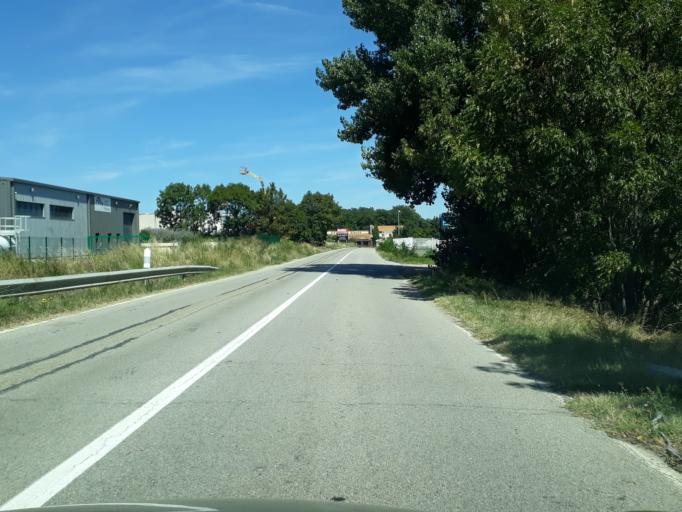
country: FR
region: Rhone-Alpes
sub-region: Departement de l'Ardeche
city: Felines
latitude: 45.3031
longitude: 4.7340
